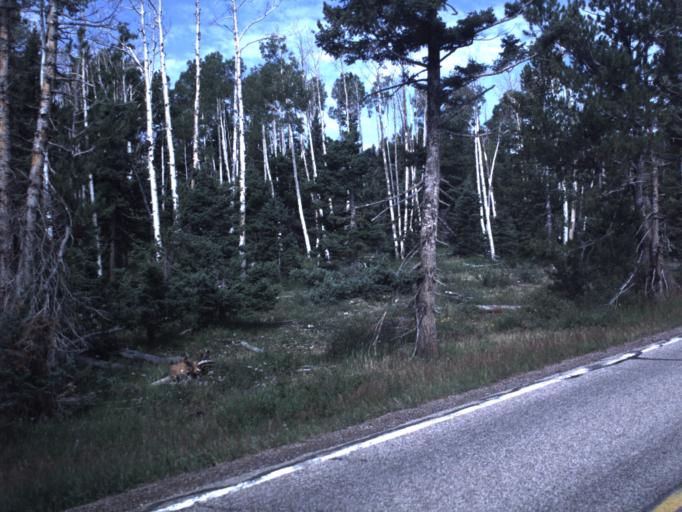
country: US
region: Utah
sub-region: Iron County
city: Parowan
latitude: 37.5289
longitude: -112.7640
